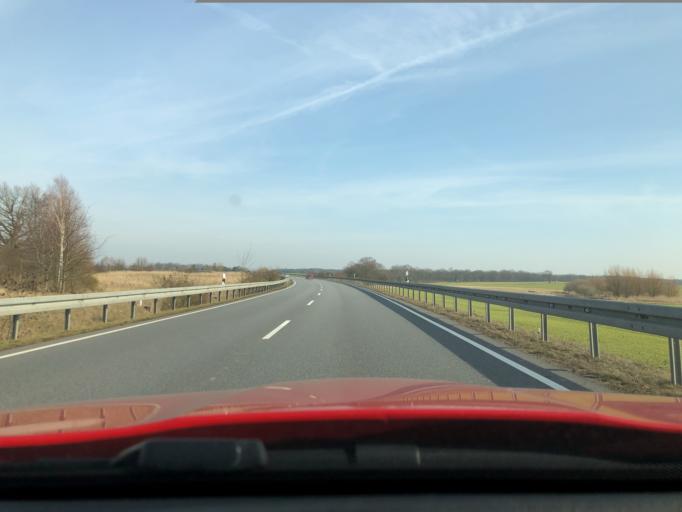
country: DE
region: Brandenburg
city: Muncheberg
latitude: 52.4940
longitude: 14.1618
